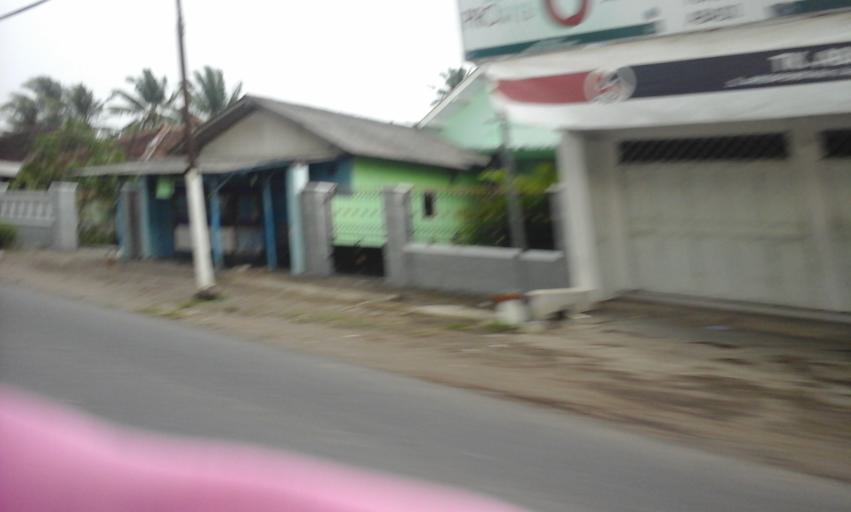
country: ID
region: East Java
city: Durenan
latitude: -8.2481
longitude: 113.6526
